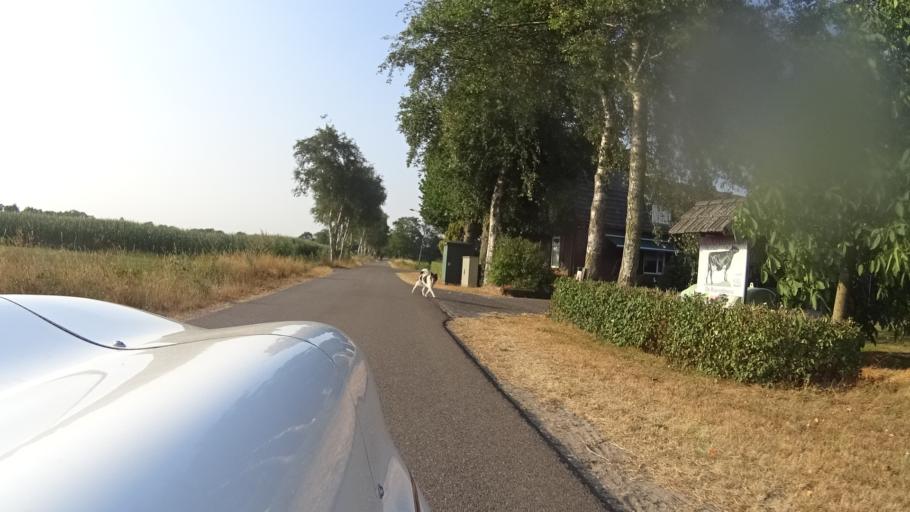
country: NL
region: North Brabant
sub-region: Gemeente Landerd
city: Zeeland
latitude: 51.7168
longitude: 5.6729
